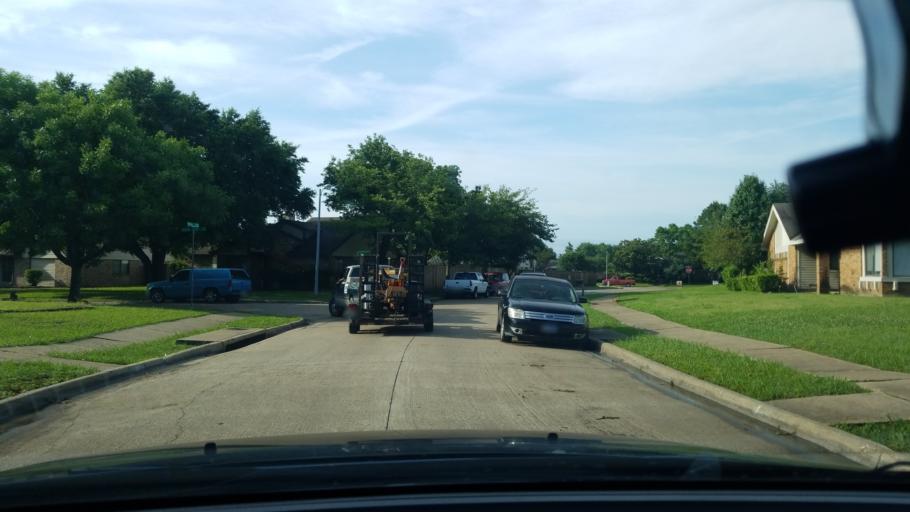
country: US
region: Texas
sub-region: Dallas County
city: Mesquite
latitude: 32.8029
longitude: -96.6049
